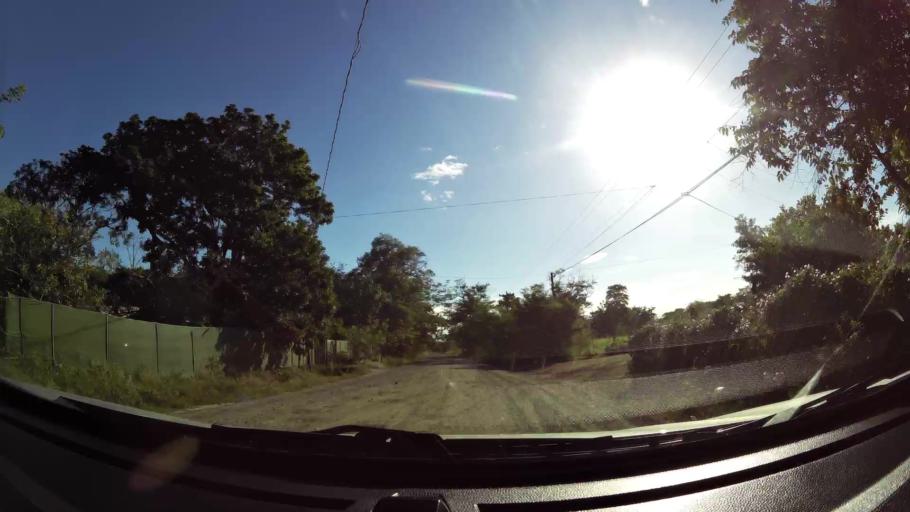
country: CR
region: Guanacaste
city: Sardinal
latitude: 10.4805
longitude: -85.6100
